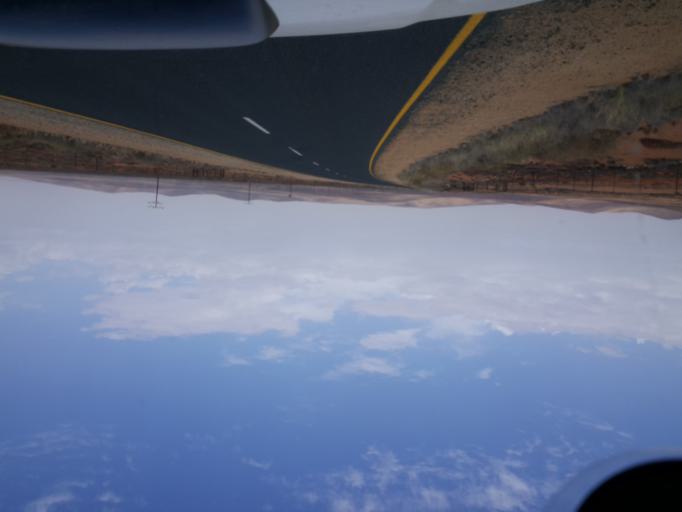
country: ZA
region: Northern Cape
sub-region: Namakwa District Municipality
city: Springbok
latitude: -29.2588
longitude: 17.4629
